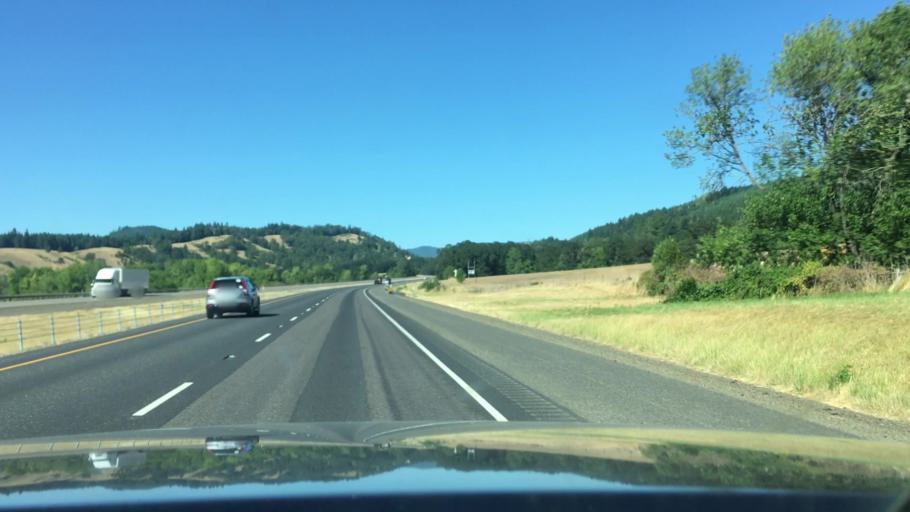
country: US
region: Oregon
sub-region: Douglas County
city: Yoncalla
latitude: 43.5887
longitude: -123.2520
